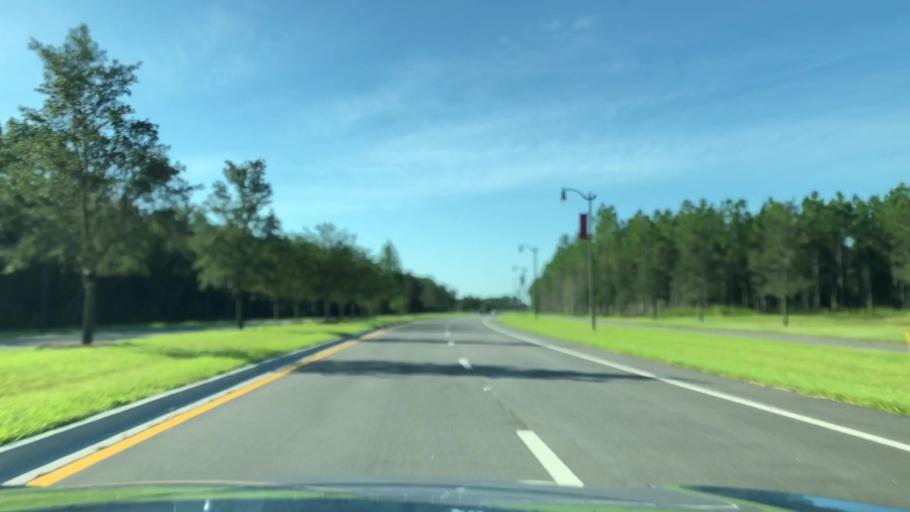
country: US
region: Florida
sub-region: Saint Johns County
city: Palm Valley
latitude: 30.0801
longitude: -81.4026
